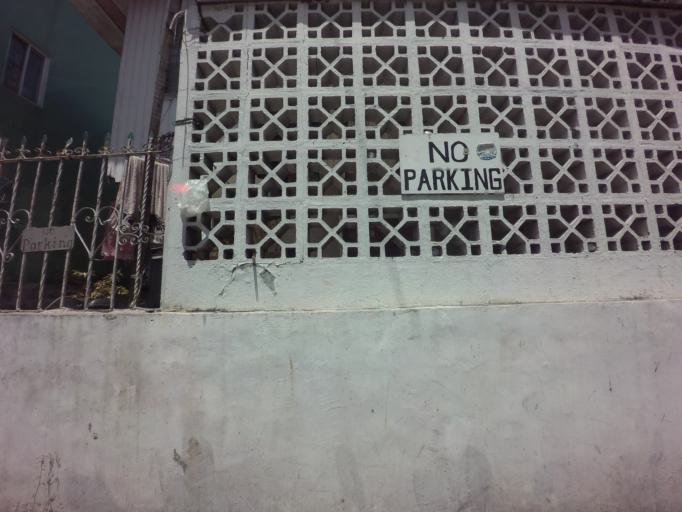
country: PH
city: Sambayanihan People's Village
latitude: 14.4979
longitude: 120.9913
